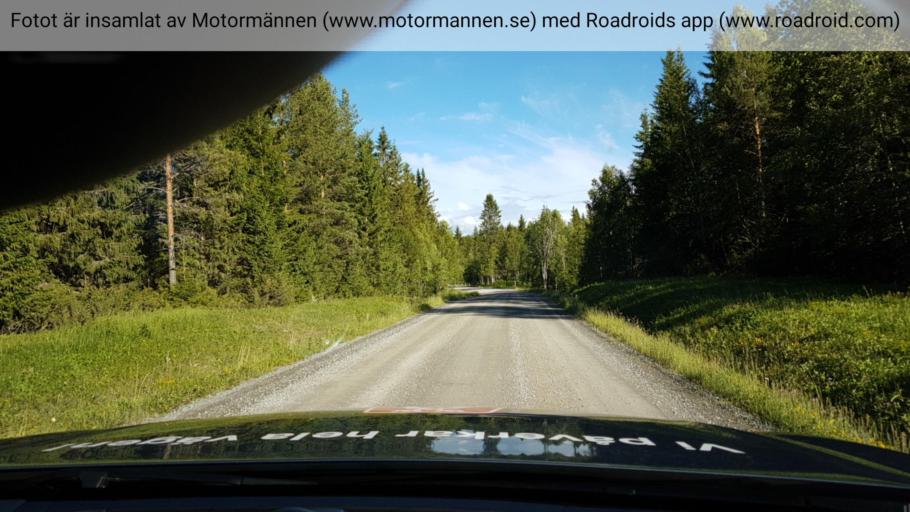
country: SE
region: Jaemtland
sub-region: Bergs Kommun
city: Hoverberg
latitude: 63.0309
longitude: 14.3558
